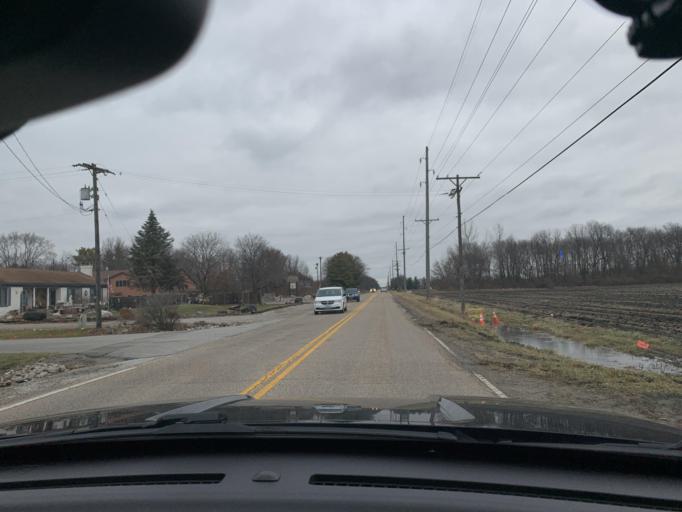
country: US
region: Illinois
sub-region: Sangamon County
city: Jerome
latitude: 39.7508
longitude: -89.6866
